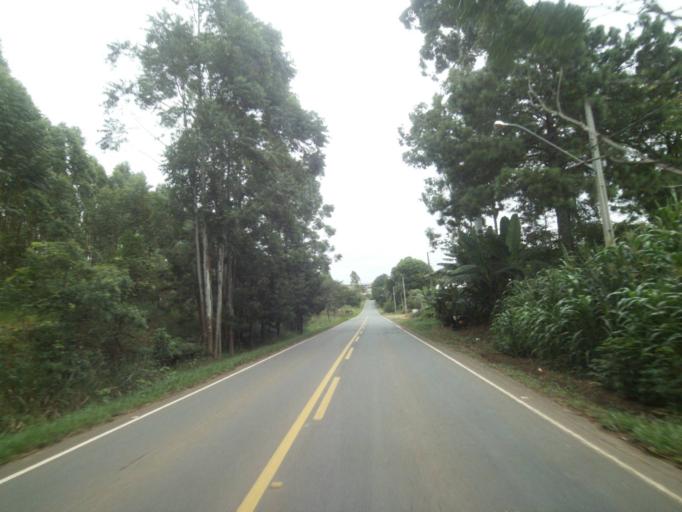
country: BR
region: Parana
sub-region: Telemaco Borba
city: Telemaco Borba
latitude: -24.3837
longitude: -50.6645
